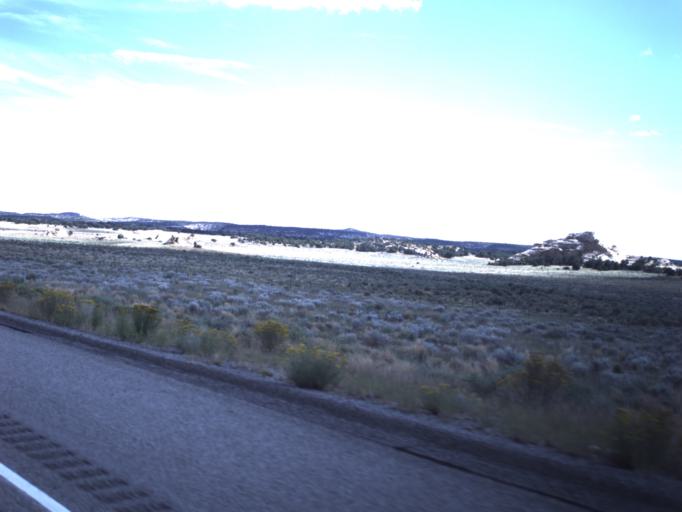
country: US
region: Utah
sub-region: Emery County
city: Ferron
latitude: 38.8646
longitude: -110.7974
